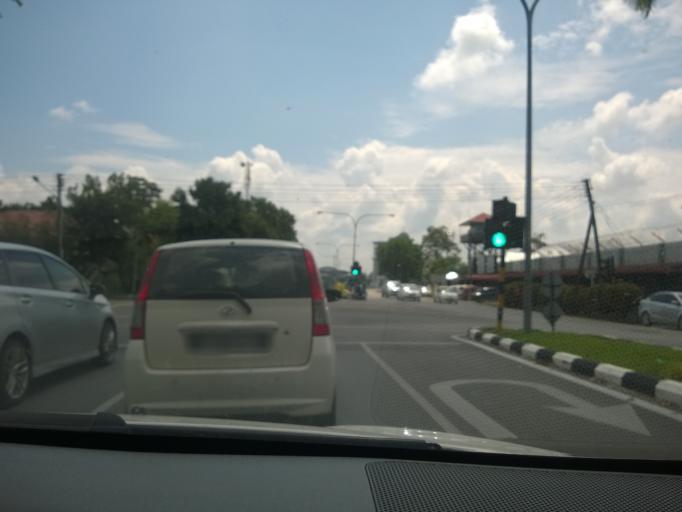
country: MY
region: Sarawak
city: Sibu
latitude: 2.2979
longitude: 111.8212
